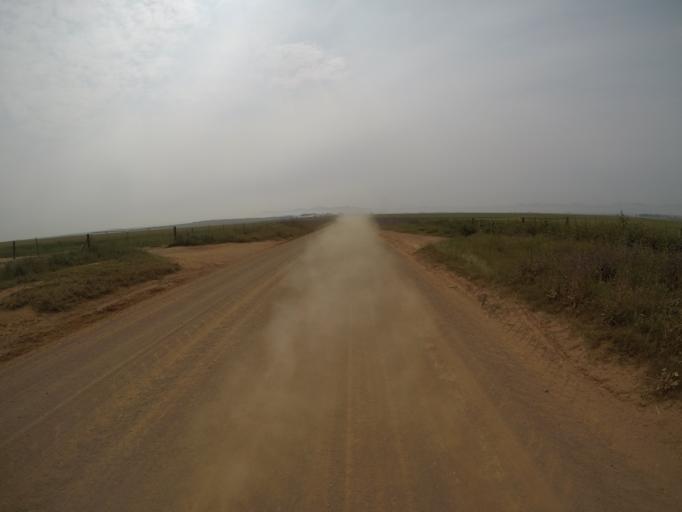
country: ZA
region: Western Cape
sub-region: City of Cape Town
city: Kraaifontein
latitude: -33.7179
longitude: 18.6799
